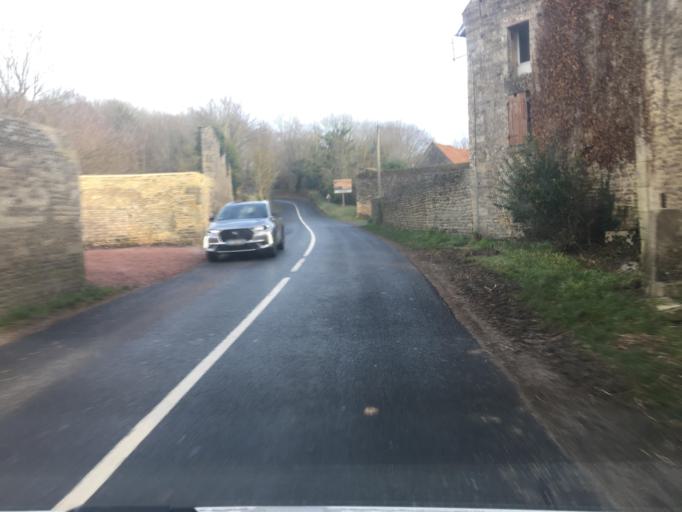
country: FR
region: Lower Normandy
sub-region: Departement du Calvados
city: Creully
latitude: 49.2895
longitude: -0.5421
